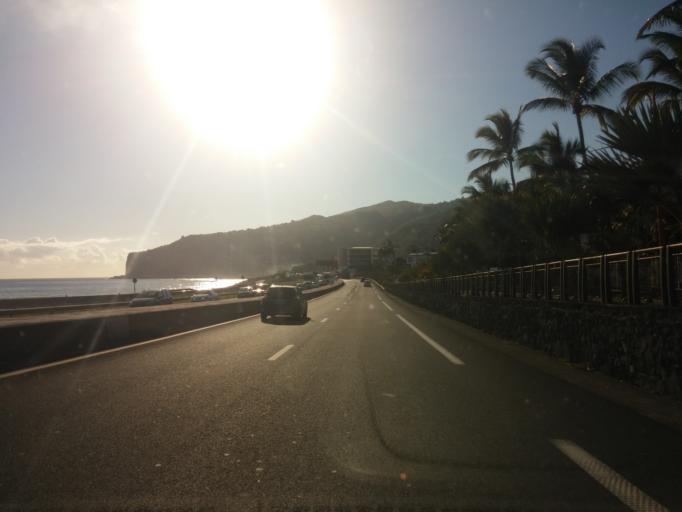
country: RE
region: Reunion
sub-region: Reunion
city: La Possession
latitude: -20.9263
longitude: 55.3353
